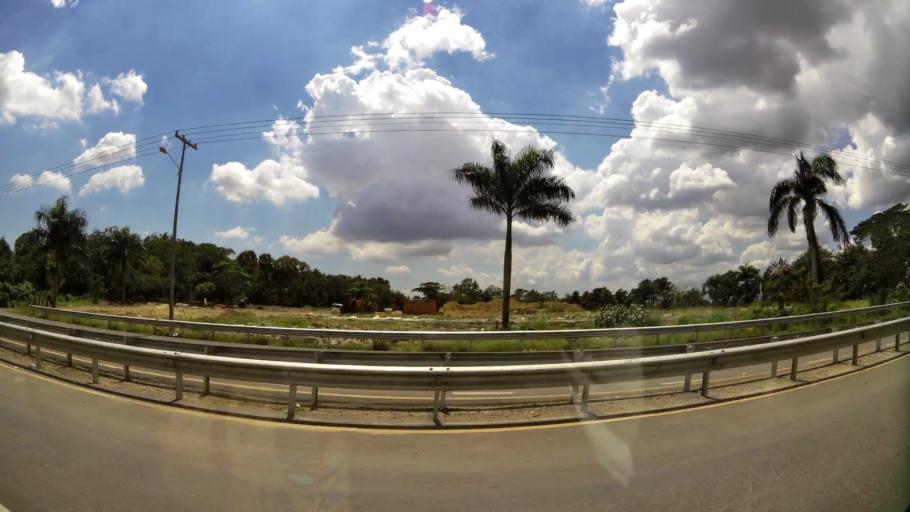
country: DO
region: Nacional
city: Santo Domingo
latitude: 18.5484
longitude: -69.9667
